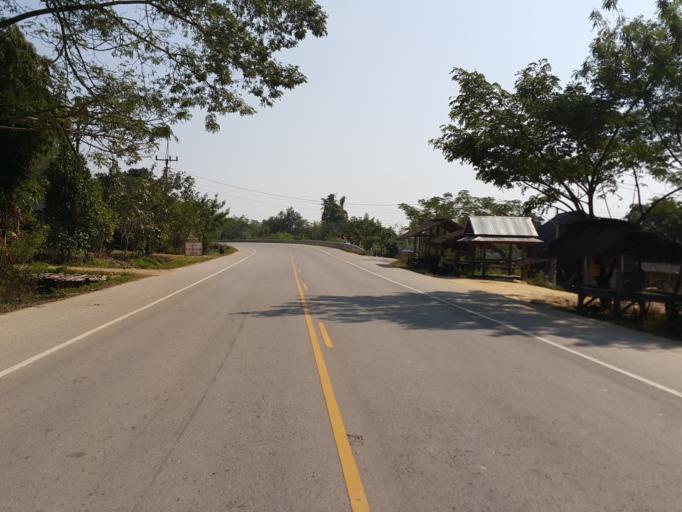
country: TH
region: Lampang
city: Mueang Pan
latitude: 18.8539
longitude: 99.5992
